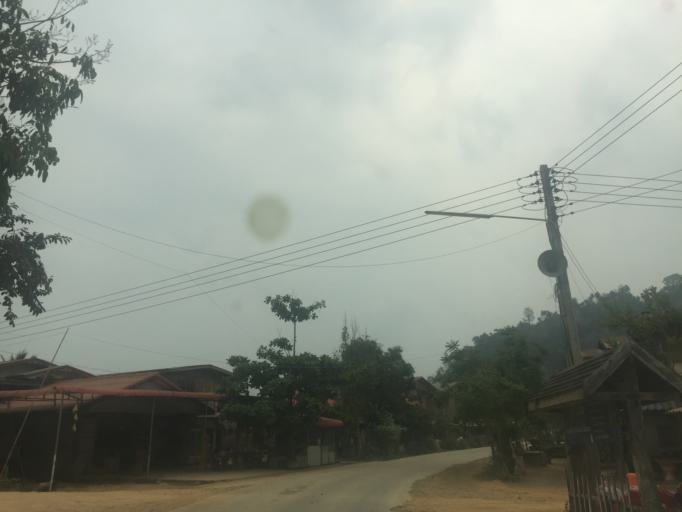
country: LA
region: Vientiane
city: Muang Sanakham
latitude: 18.3898
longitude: 101.5215
